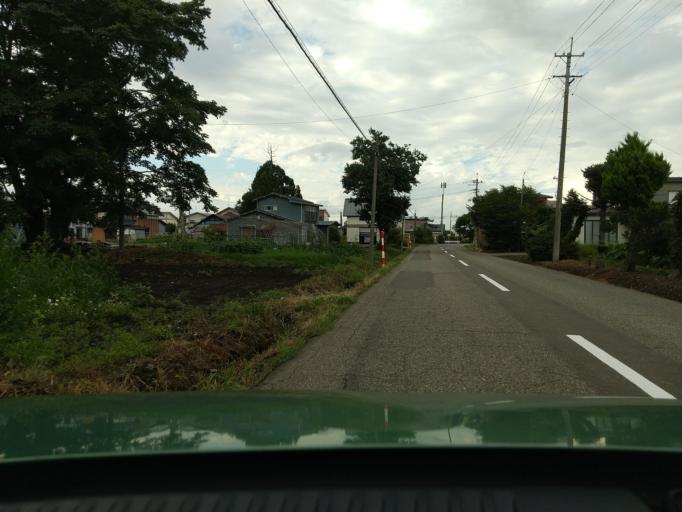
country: JP
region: Akita
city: Yokotemachi
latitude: 39.2897
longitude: 140.4812
